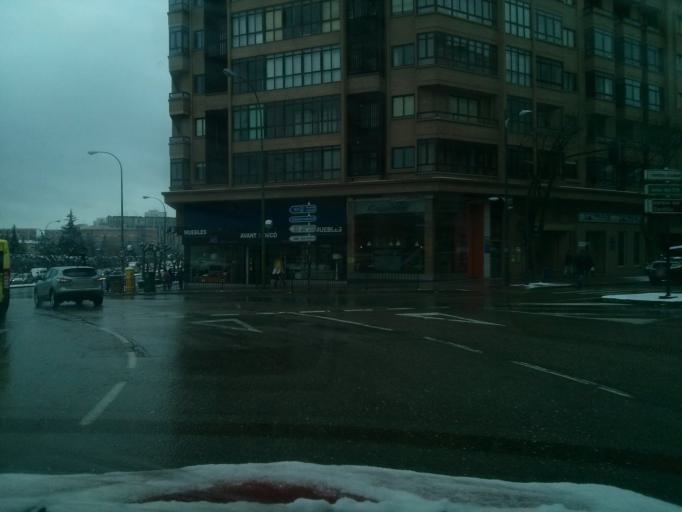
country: ES
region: Castille and Leon
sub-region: Provincia de Burgos
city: Burgos
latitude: 42.3544
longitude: -3.6918
